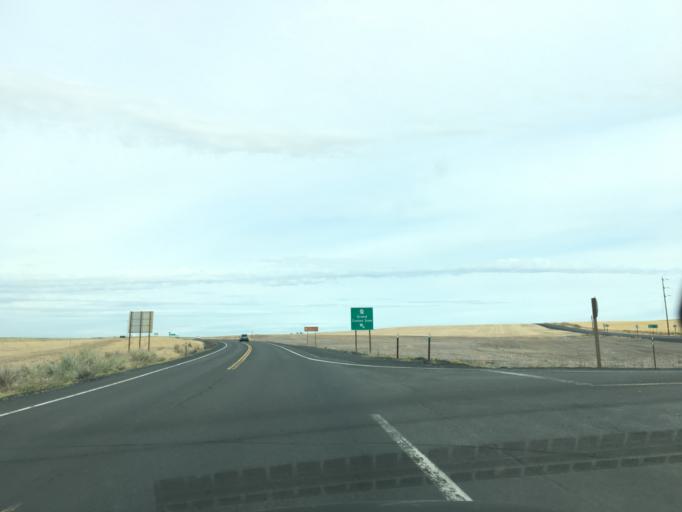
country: US
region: Washington
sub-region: Okanogan County
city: Coulee Dam
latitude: 47.7706
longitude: -118.7224
